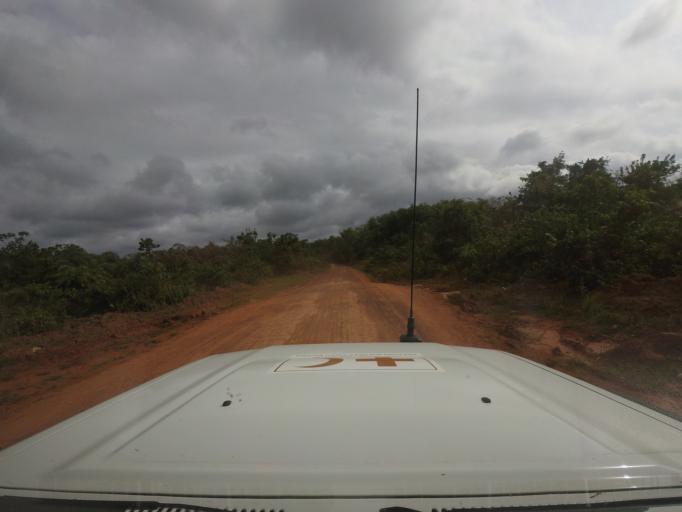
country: LR
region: Bong
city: Gbarnga
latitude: 7.0344
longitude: -9.4667
